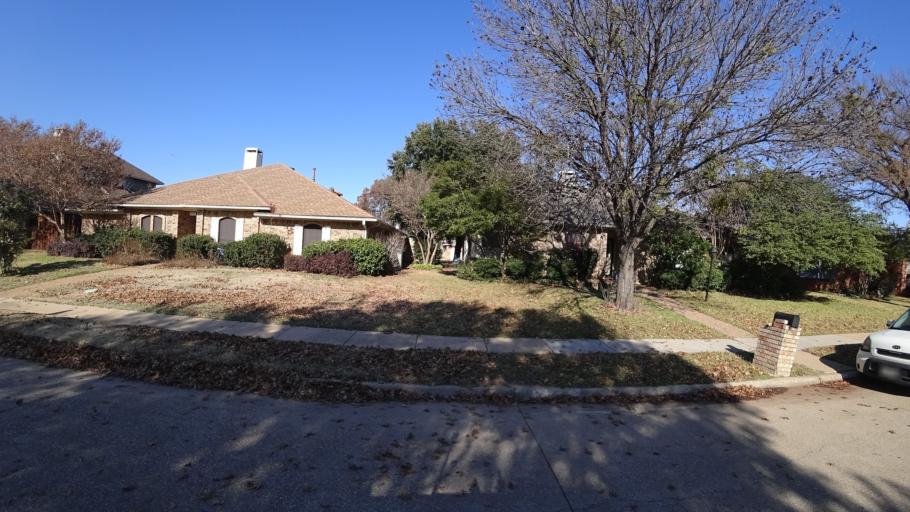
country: US
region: Texas
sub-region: Denton County
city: Lewisville
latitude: 33.0167
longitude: -97.0254
